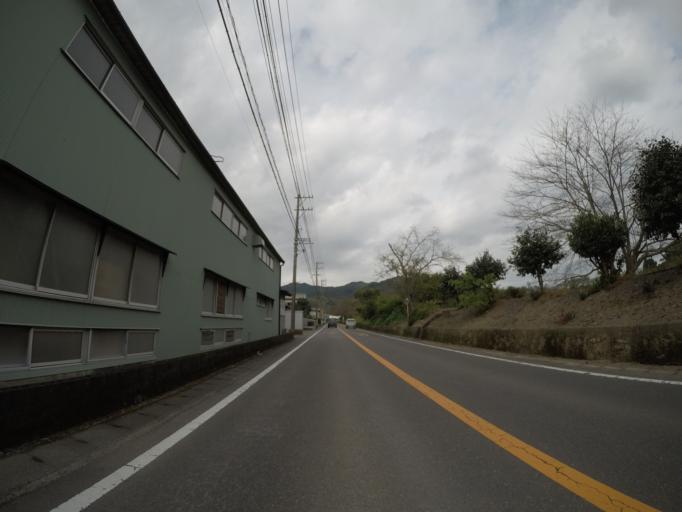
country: JP
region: Shizuoka
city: Fujieda
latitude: 34.8884
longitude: 138.2160
